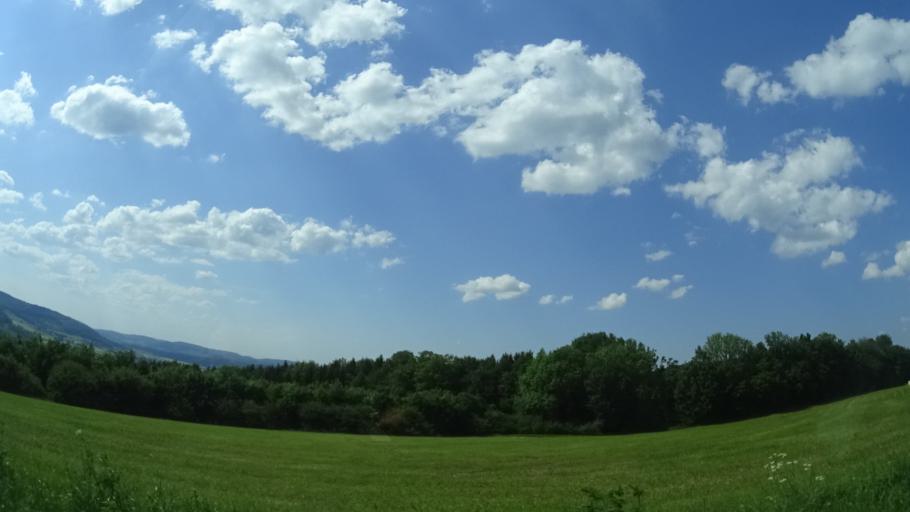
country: DE
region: Hesse
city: Tann
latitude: 50.6536
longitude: 10.0362
